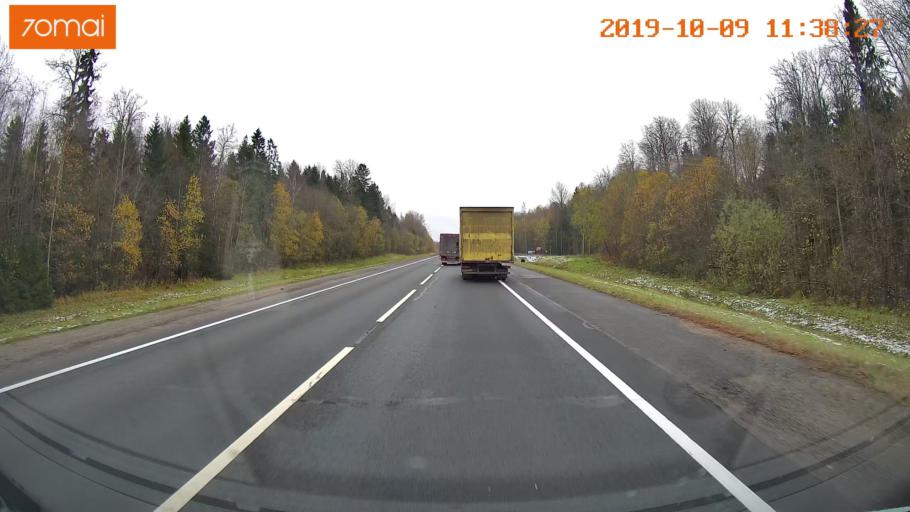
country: RU
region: Vologda
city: Gryazovets
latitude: 58.9681
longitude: 40.1559
